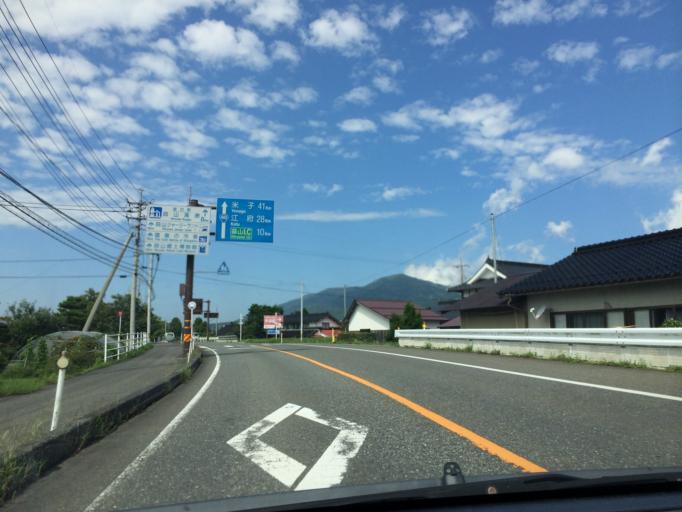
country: JP
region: Tottori
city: Kurayoshi
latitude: 35.2914
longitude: 133.7322
